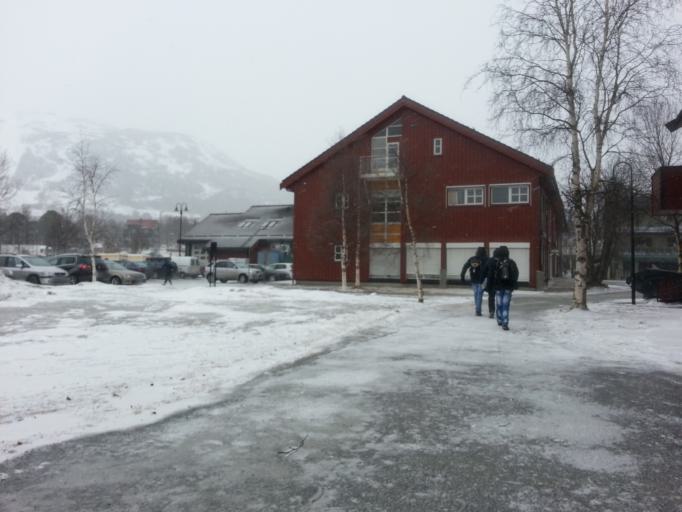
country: NO
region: Sor-Trondelag
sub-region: Oppdal
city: Oppdal
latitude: 62.5941
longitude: 9.6887
